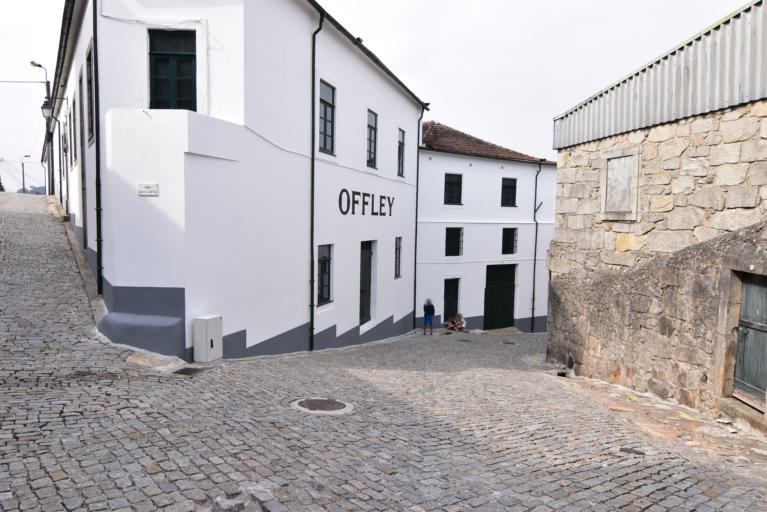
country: PT
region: Porto
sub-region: Vila Nova de Gaia
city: Vila Nova de Gaia
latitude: 41.1352
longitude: -8.6143
